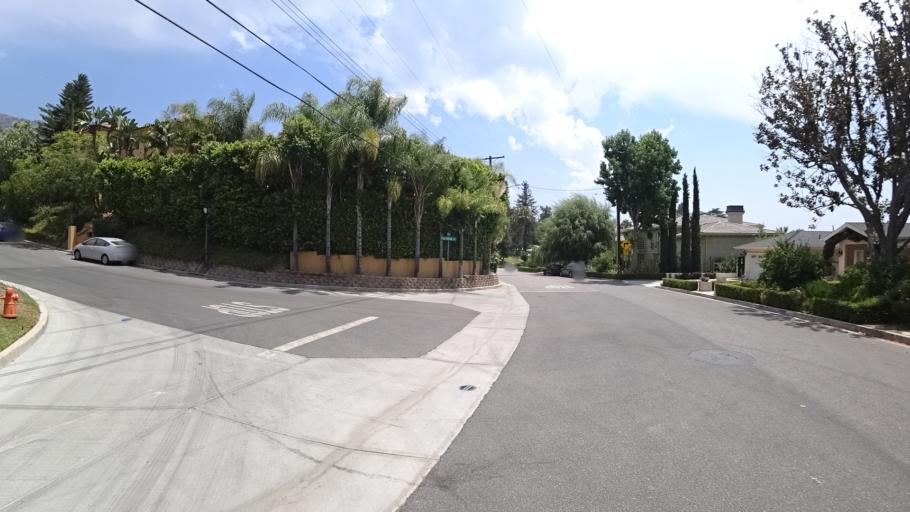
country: US
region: California
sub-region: Los Angeles County
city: Burbank
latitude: 34.1872
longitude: -118.2854
